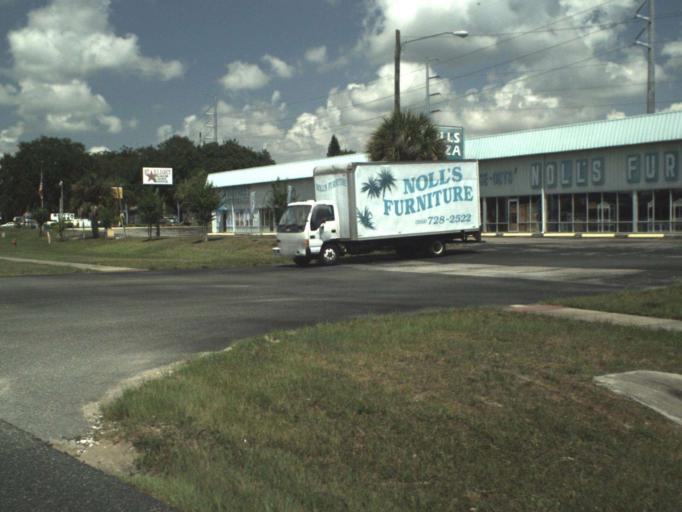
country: US
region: Florida
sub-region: Lake County
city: Leesburg
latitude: 28.8192
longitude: -81.8397
